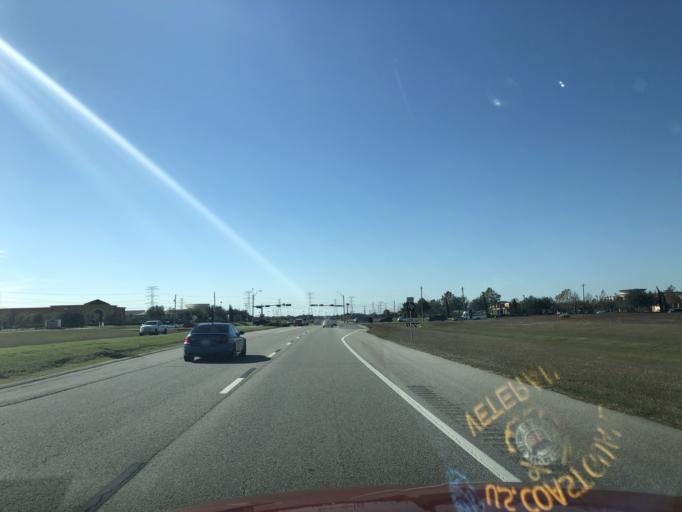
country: US
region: Texas
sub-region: Galveston County
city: League City
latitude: 29.4959
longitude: -95.0617
